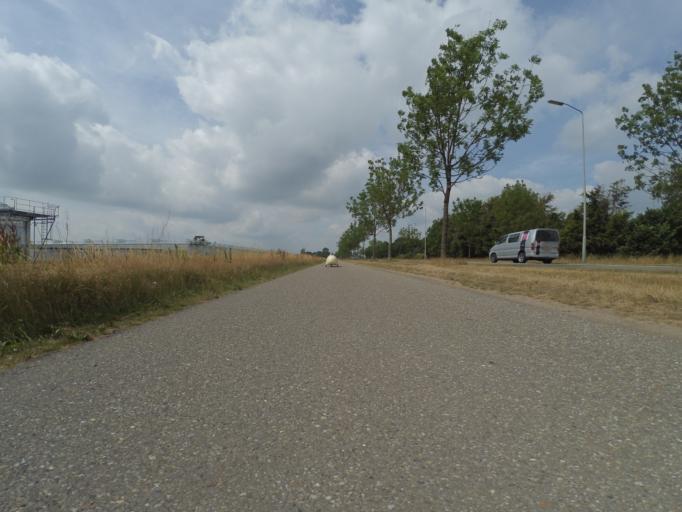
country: NL
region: North Brabant
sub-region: Gemeente Made en Drimmelen
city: Drimmelen
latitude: 51.6923
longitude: 4.8174
